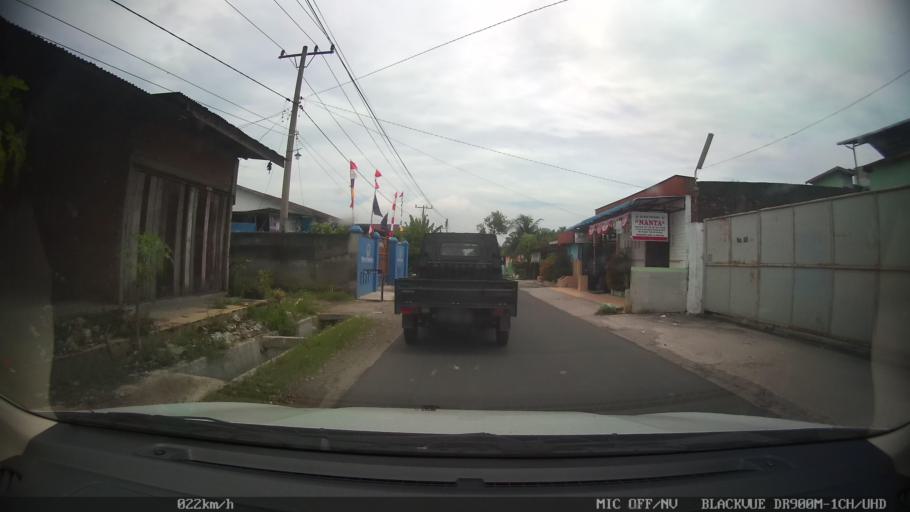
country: ID
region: North Sumatra
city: Binjai
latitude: 3.6091
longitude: 98.5539
